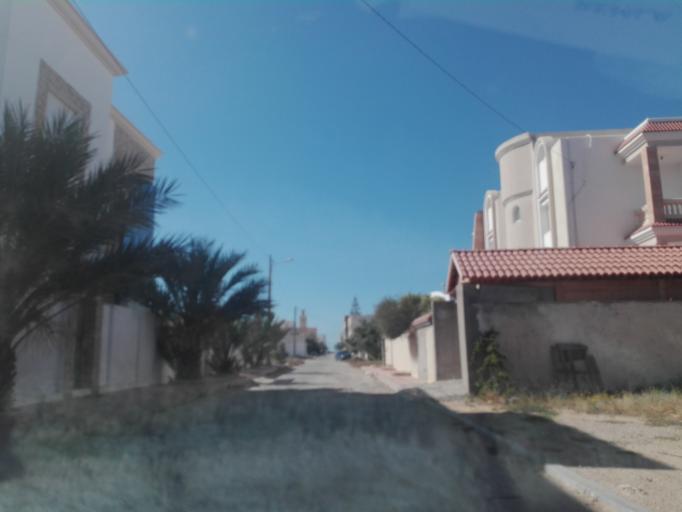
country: TN
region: Safaqis
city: Al Qarmadah
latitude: 34.7076
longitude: 11.2009
